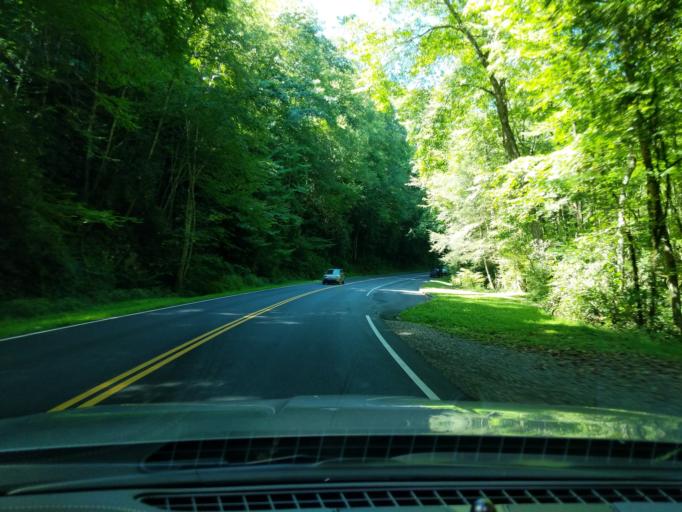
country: US
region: North Carolina
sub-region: Swain County
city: Cherokee
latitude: 35.5771
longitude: -83.3449
